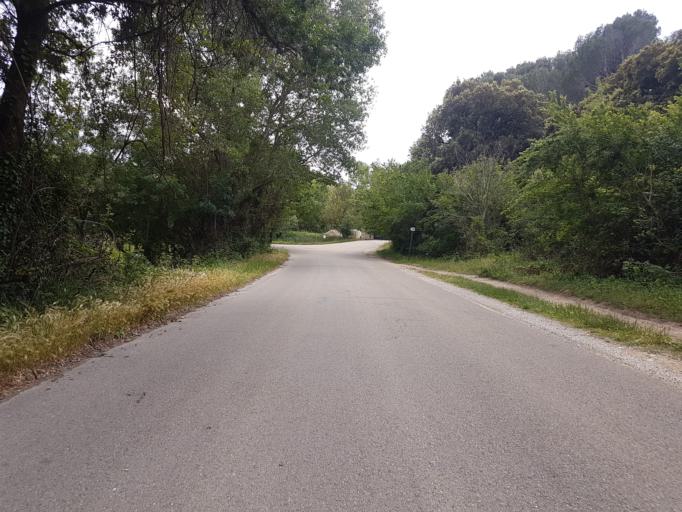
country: FR
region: Languedoc-Roussillon
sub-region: Departement du Gard
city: Beaucaire
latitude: 43.8167
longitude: 4.6402
